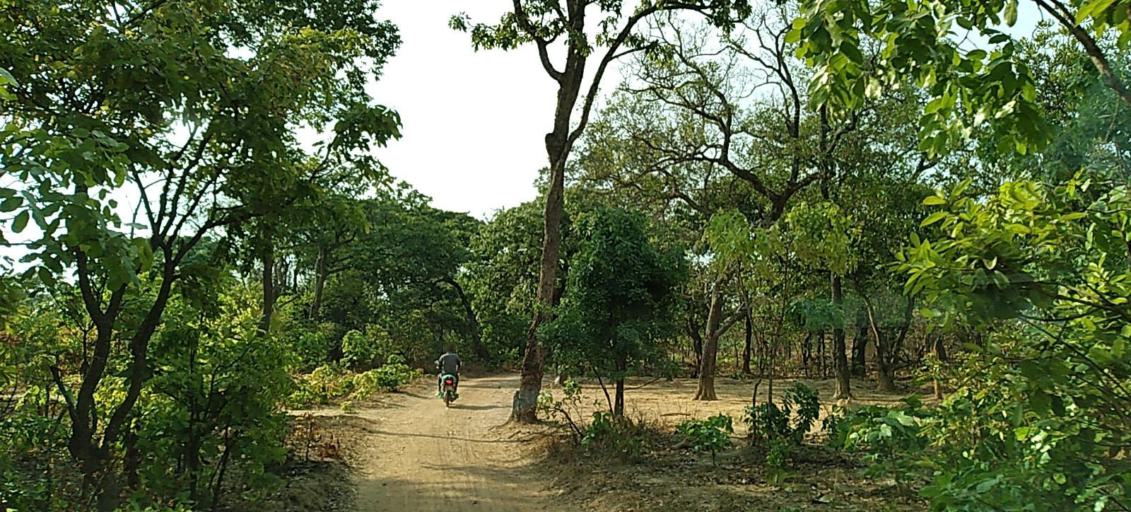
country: ZM
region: Copperbelt
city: Kalulushi
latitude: -12.9607
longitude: 27.6997
